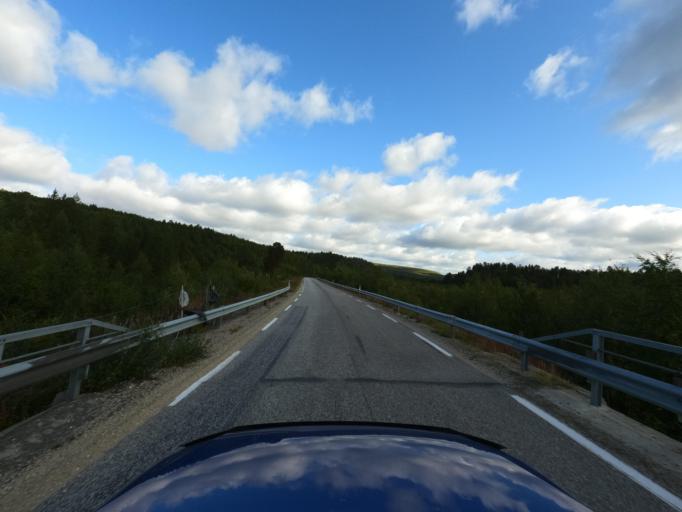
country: NO
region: Finnmark Fylke
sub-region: Porsanger
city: Lakselv
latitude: 69.4239
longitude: 24.8544
